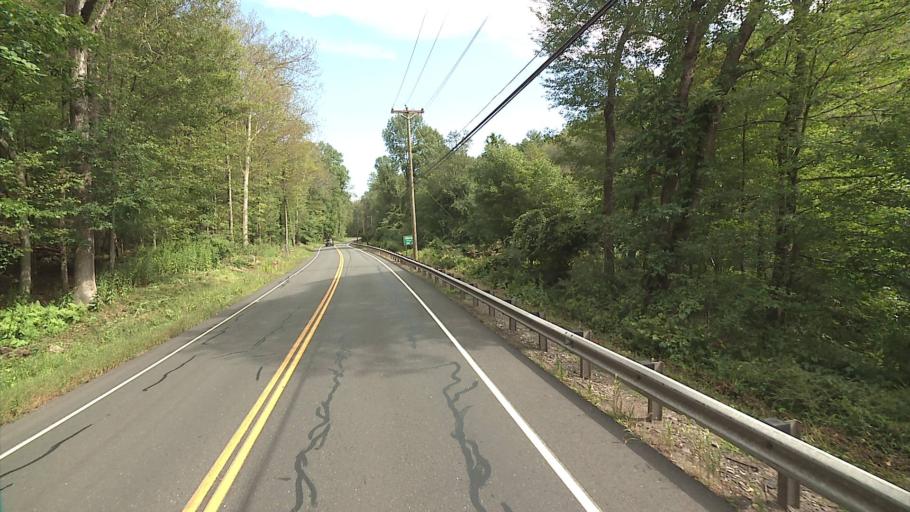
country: US
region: Connecticut
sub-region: Tolland County
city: Stafford Springs
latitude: 41.9405
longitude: -72.3069
